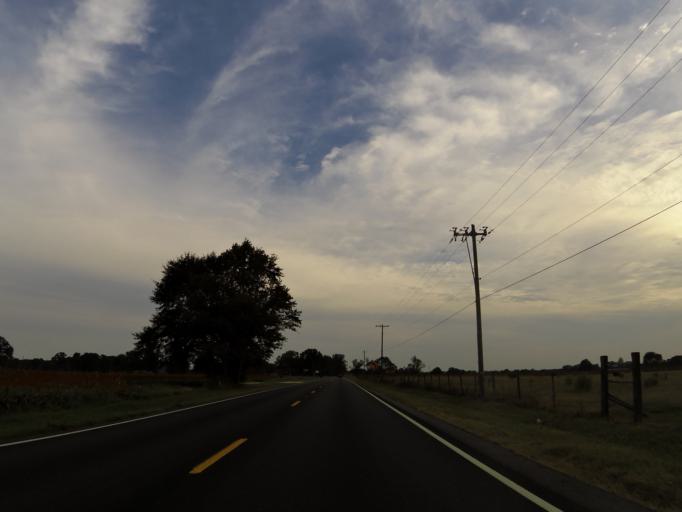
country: US
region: Alabama
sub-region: Escambia County
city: Atmore
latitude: 31.2060
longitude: -87.4682
